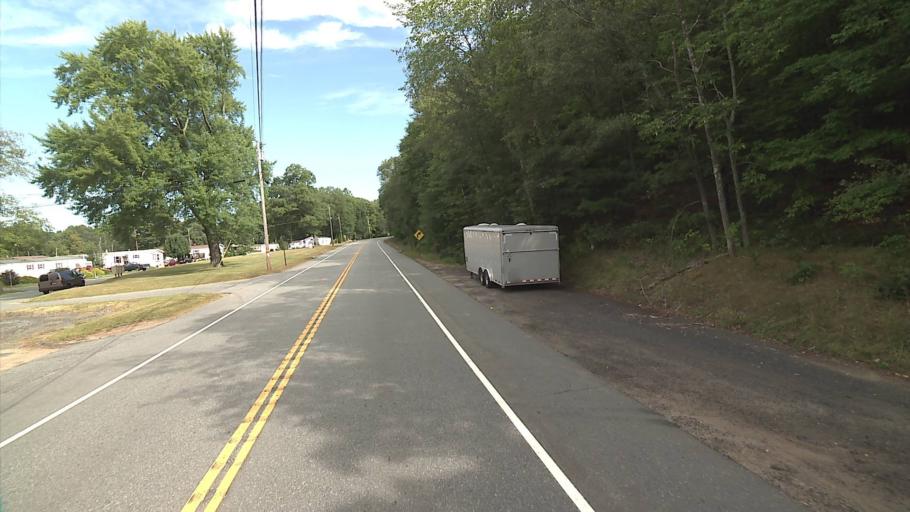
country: US
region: Connecticut
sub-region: Tolland County
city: South Coventry
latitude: 41.8246
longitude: -72.3106
